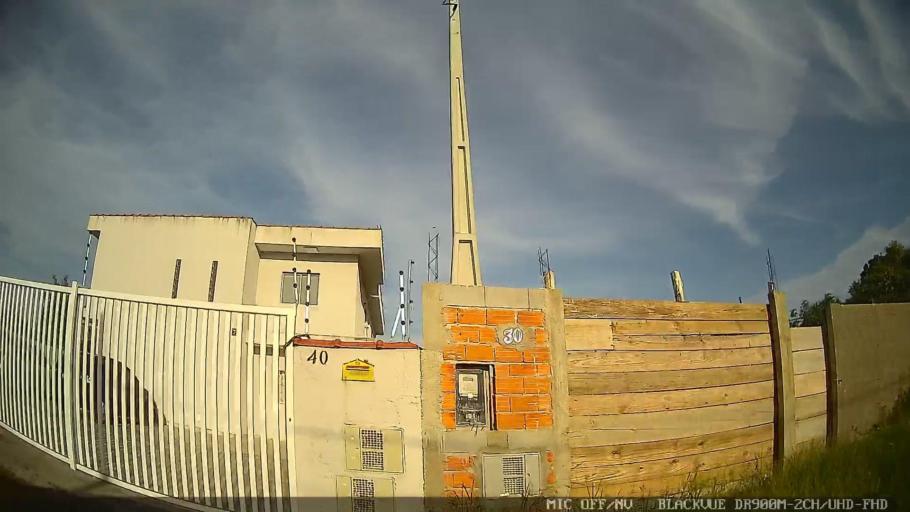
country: BR
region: Sao Paulo
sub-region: Itanhaem
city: Itanhaem
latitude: -24.1599
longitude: -46.7719
